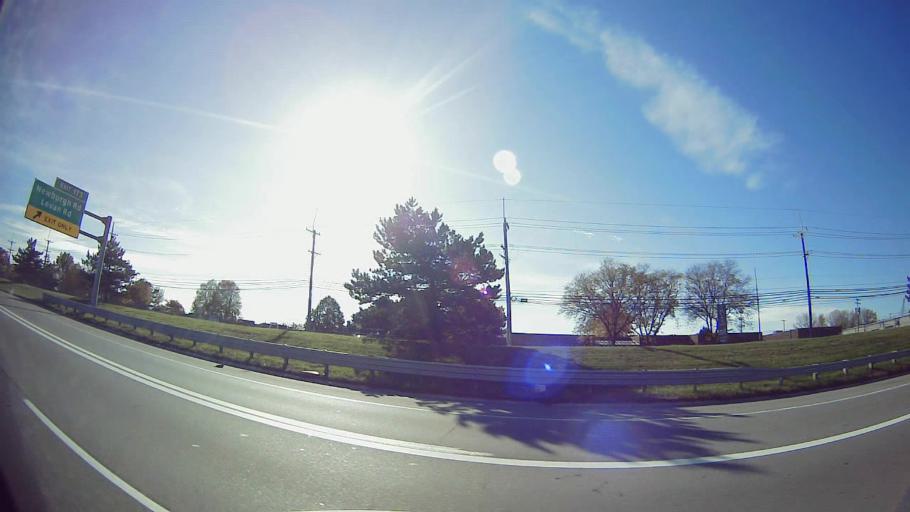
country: US
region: Michigan
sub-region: Wayne County
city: Plymouth
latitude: 42.3816
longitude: -83.4197
